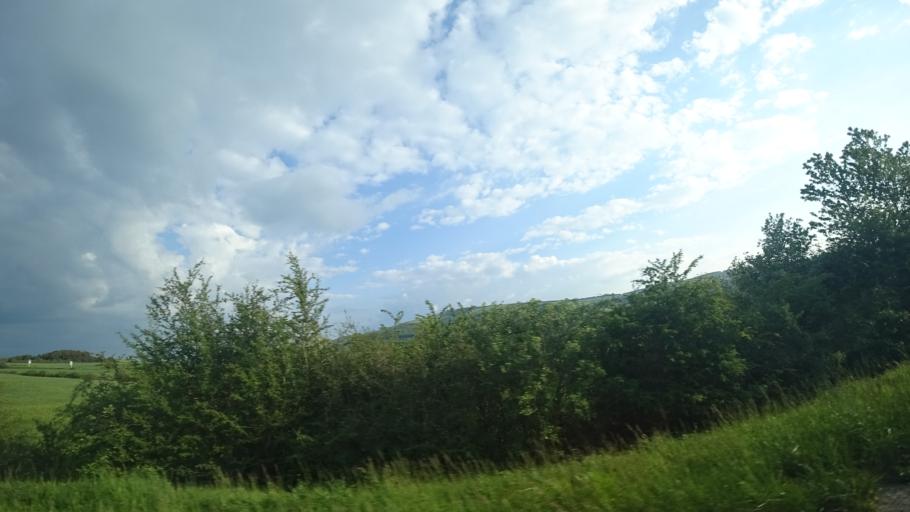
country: FR
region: Midi-Pyrenees
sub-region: Departement de l'Aveyron
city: Severac-le-Chateau
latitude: 44.2433
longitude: 2.9380
